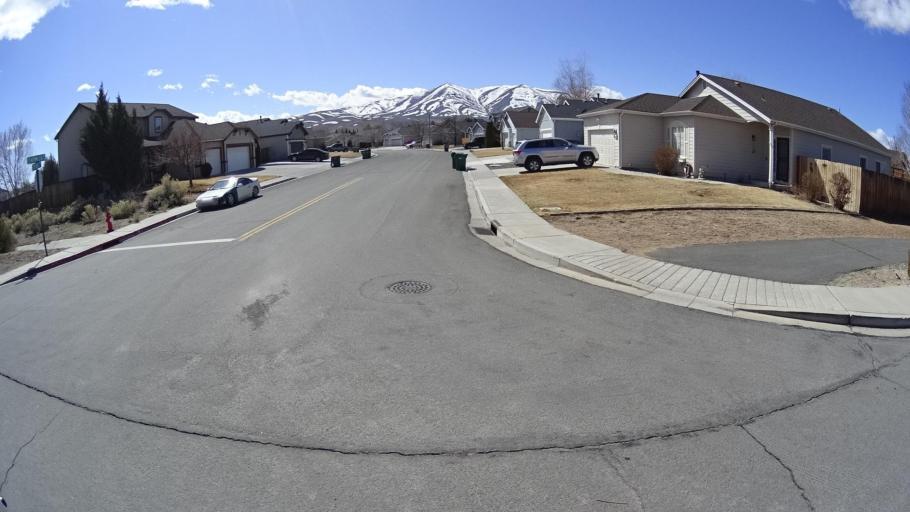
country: US
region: Nevada
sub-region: Washoe County
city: Lemmon Valley
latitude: 39.6349
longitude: -119.8666
